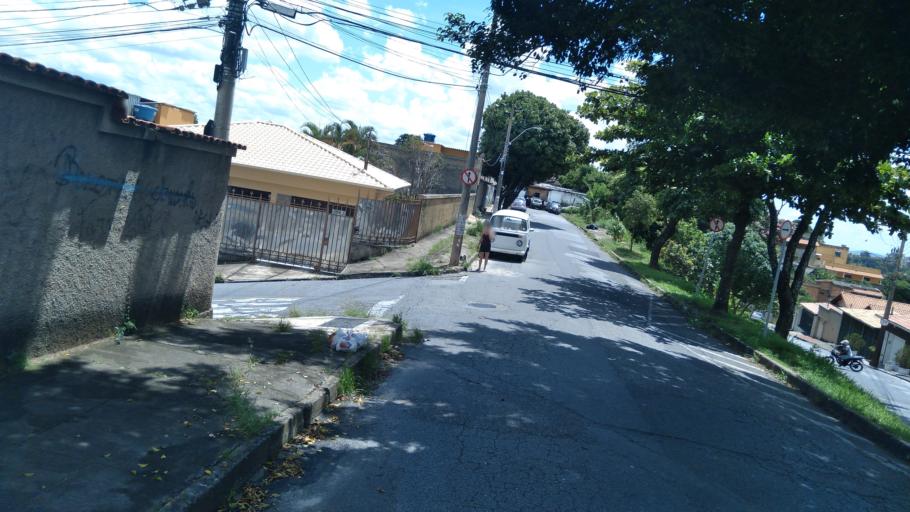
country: BR
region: Minas Gerais
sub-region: Belo Horizonte
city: Belo Horizonte
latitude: -19.8650
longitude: -43.9147
